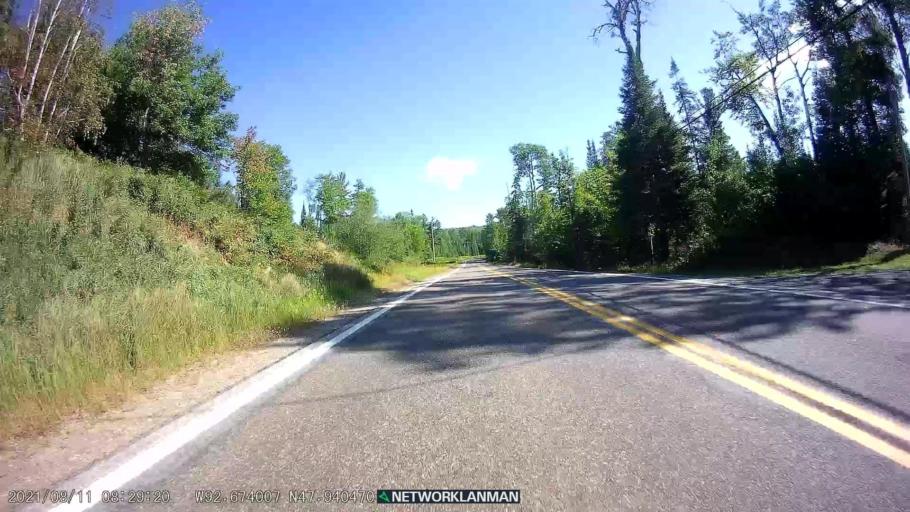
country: US
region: Minnesota
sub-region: Saint Louis County
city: Mountain Iron
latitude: 47.9403
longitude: -92.6742
